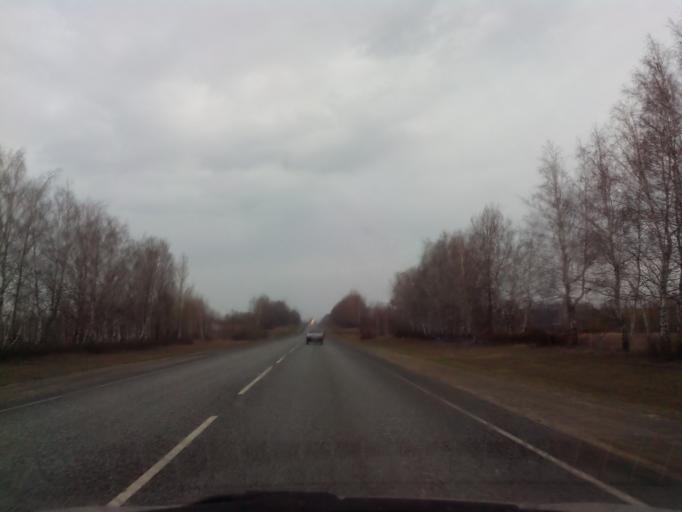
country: RU
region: Tambov
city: Pervomayskiy
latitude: 53.1454
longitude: 40.3751
